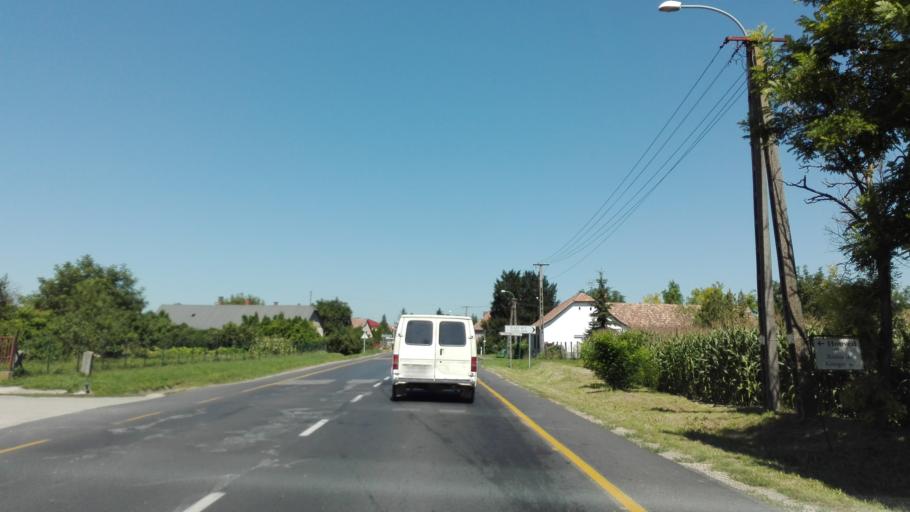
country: HU
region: Fejer
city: Mezoszilas
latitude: 46.8058
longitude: 18.4866
